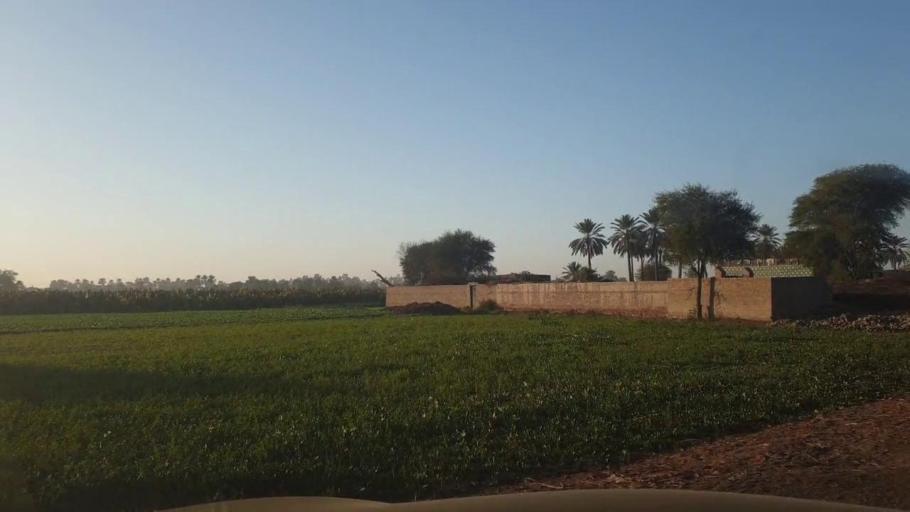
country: PK
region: Sindh
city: Ghotki
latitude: 28.0681
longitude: 69.3546
